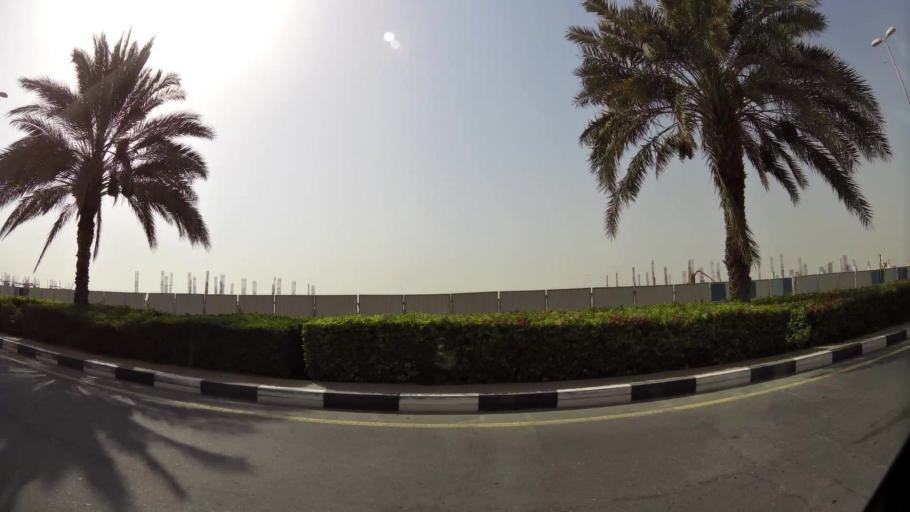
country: AE
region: Ash Shariqah
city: Sharjah
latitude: 25.2641
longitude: 55.4452
